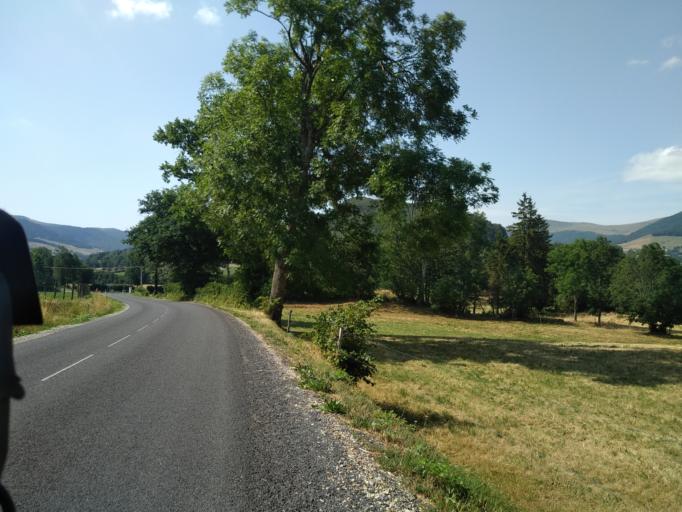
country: FR
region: Auvergne
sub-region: Departement du Cantal
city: Riom-es-Montagnes
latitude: 45.1897
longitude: 2.7152
